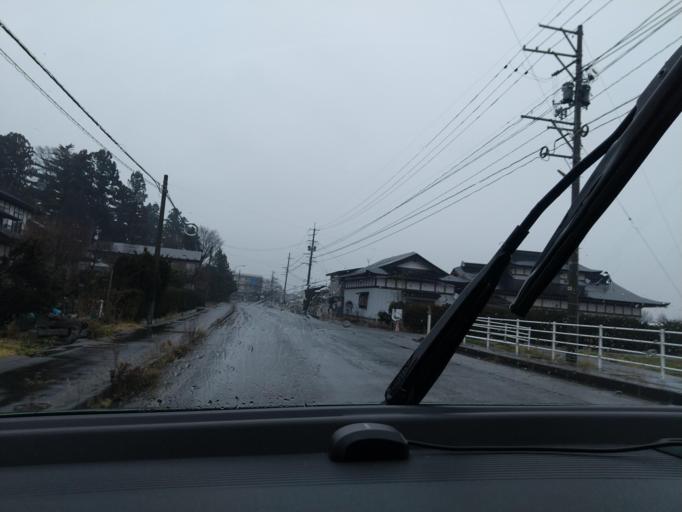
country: JP
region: Iwate
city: Morioka-shi
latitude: 39.6826
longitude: 141.1154
